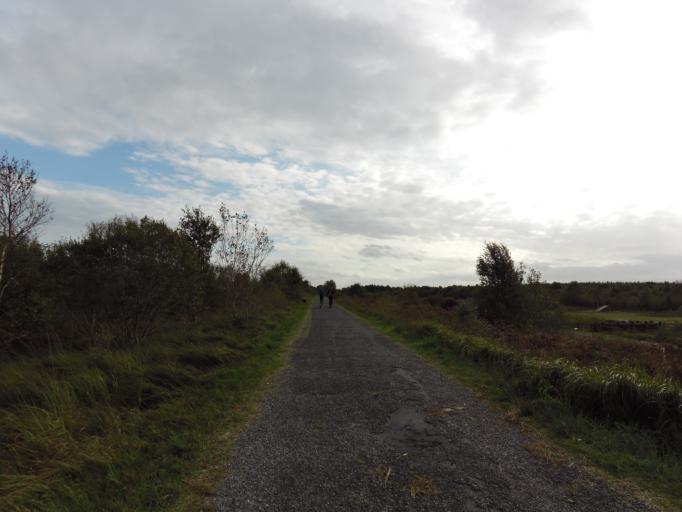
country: IE
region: Leinster
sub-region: Uibh Fhaili
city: Ferbane
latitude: 53.2197
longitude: -7.7325
